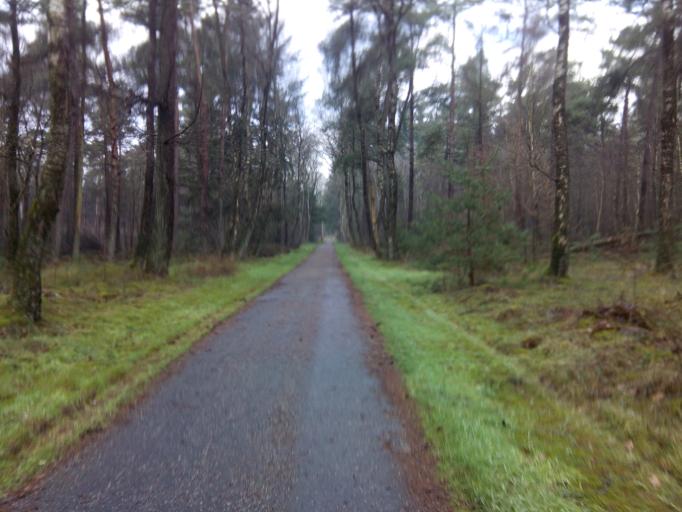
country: NL
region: Utrecht
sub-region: Gemeente Utrechtse Heuvelrug
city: Overberg
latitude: 52.0131
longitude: 5.4980
